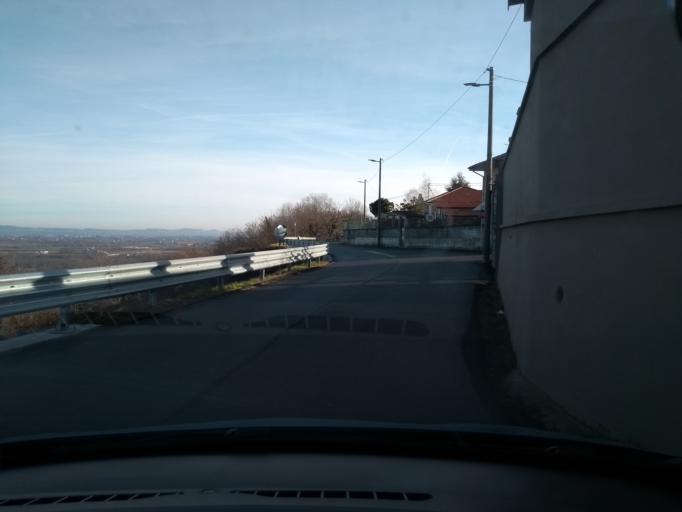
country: IT
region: Piedmont
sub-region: Provincia di Torino
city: Barbania
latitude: 45.2847
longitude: 7.6419
